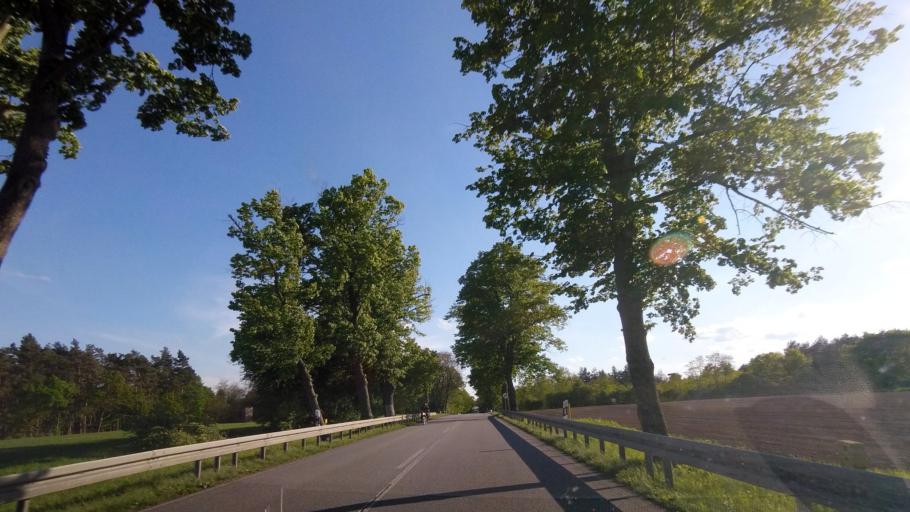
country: DE
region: Brandenburg
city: Luebben
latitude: 51.9210
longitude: 13.8727
